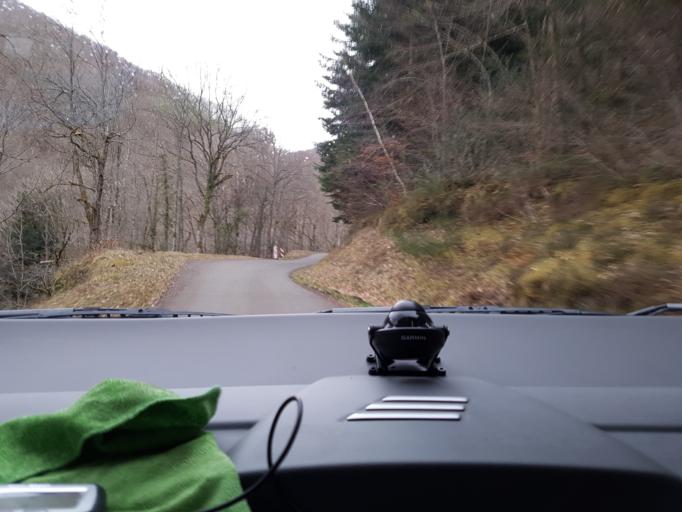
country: FR
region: Auvergne
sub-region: Departement du Puy-de-Dome
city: Chapdes-Beaufort
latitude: 45.8637
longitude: 2.8524
